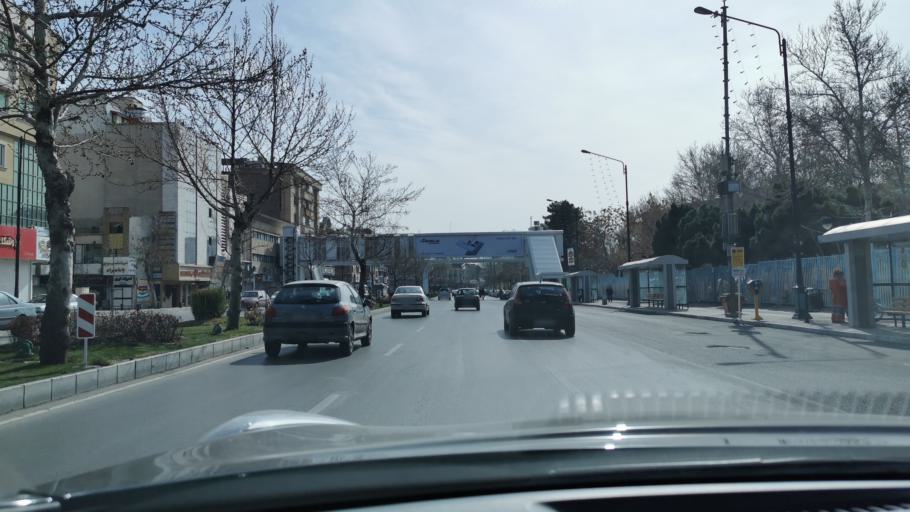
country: IR
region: Razavi Khorasan
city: Mashhad
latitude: 36.2930
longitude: 59.5822
